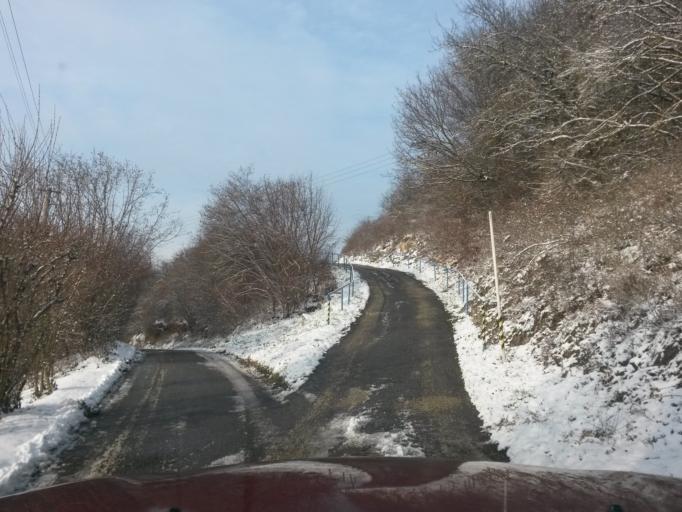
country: SK
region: Kosicky
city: Kosice
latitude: 48.8070
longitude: 21.2392
